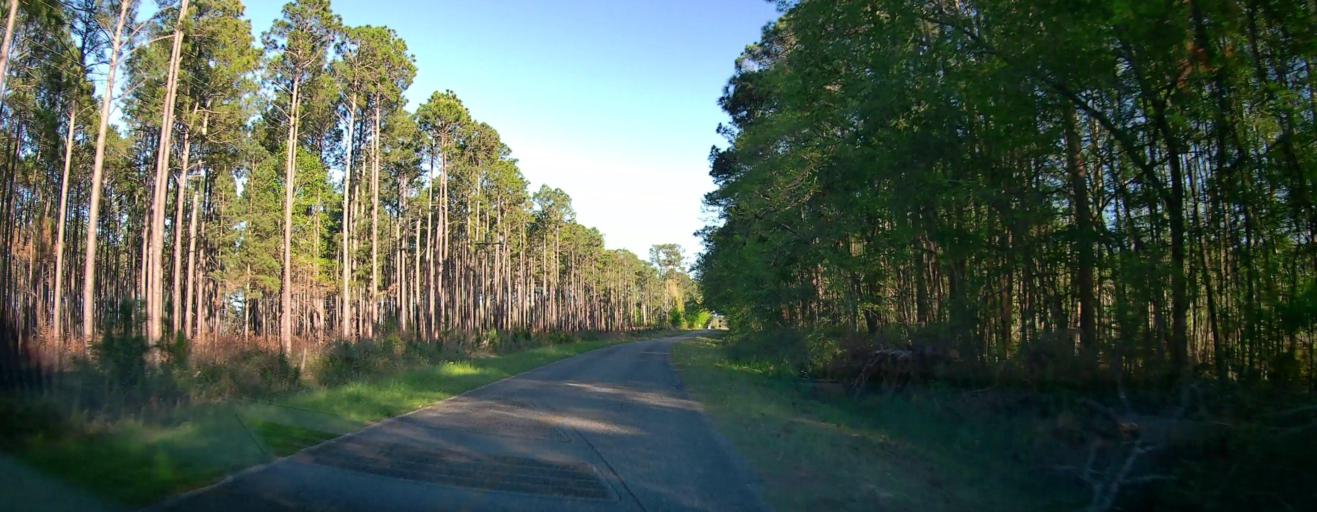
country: US
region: Georgia
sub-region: Ben Hill County
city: Fitzgerald
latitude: 31.6863
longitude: -83.1499
